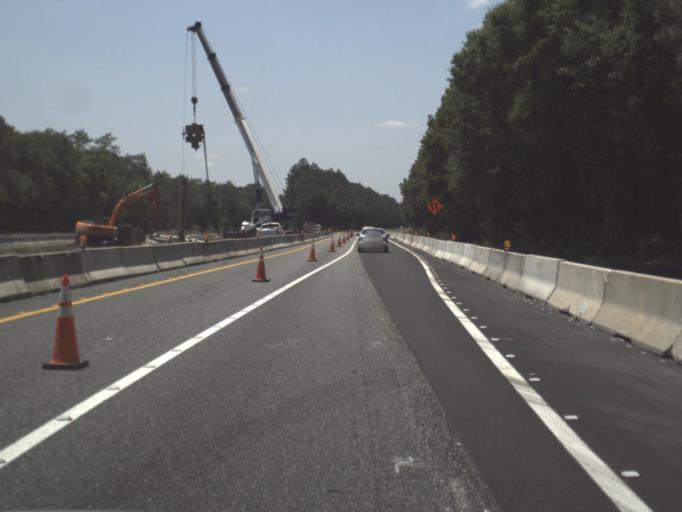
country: US
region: Florida
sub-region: Columbia County
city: Watertown
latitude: 30.2431
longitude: -82.5751
